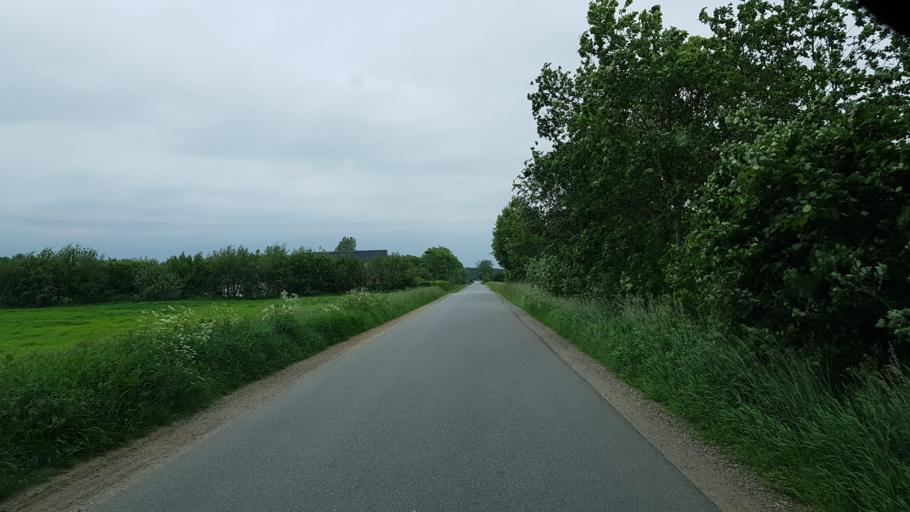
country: DK
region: South Denmark
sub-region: Varde Kommune
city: Olgod
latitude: 55.6782
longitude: 8.7425
